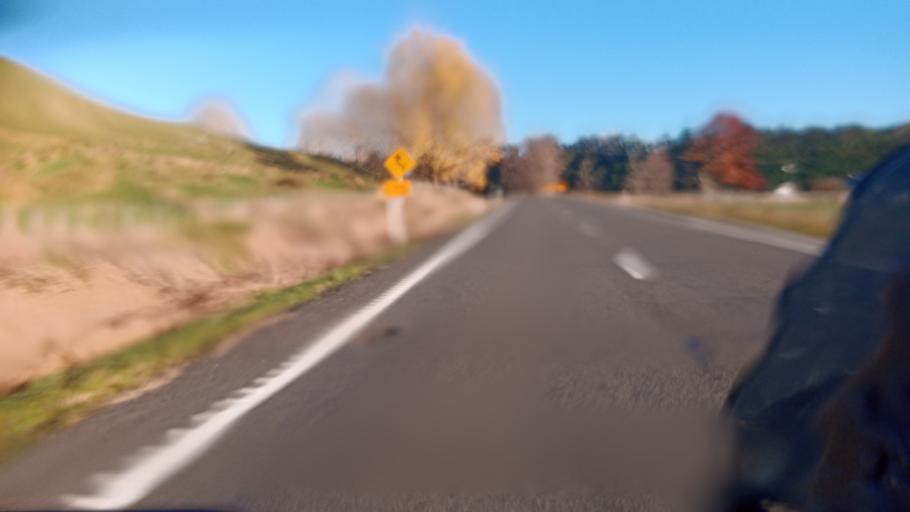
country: NZ
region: Hawke's Bay
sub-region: Wairoa District
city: Wairoa
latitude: -39.0161
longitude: 177.3571
